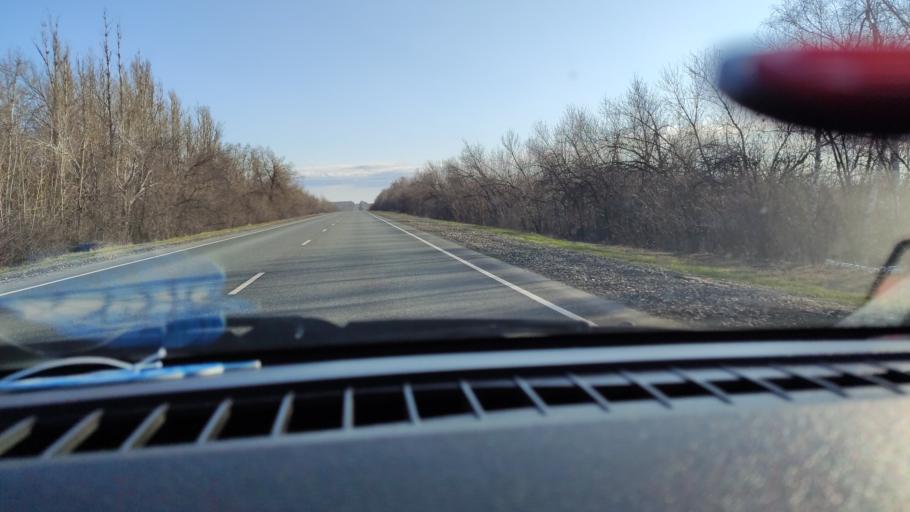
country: RU
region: Saratov
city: Khvalynsk
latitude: 52.5990
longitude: 48.1421
